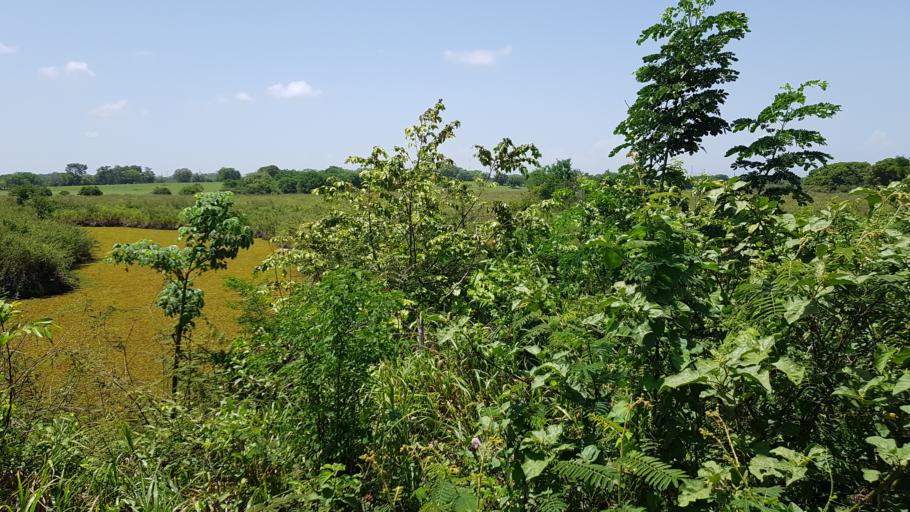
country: MX
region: Chiapas
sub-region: Catazaja
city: Catazaja
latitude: 17.7223
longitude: -92.0274
